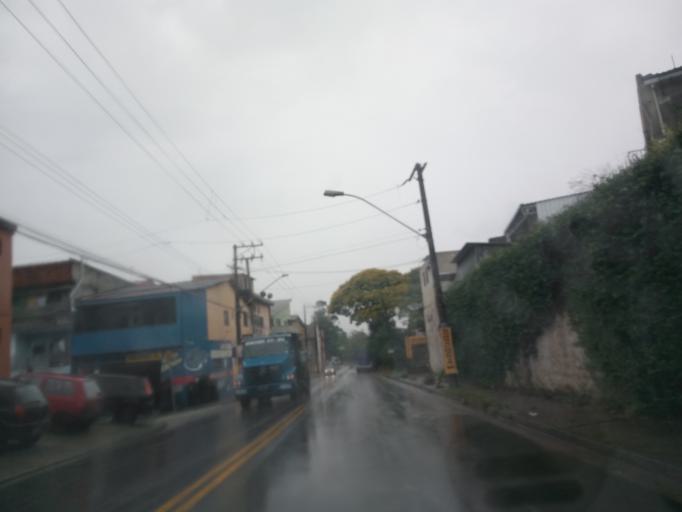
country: BR
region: Sao Paulo
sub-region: Sao Bernardo Do Campo
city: Sao Bernardo do Campo
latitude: -23.7189
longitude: -46.5953
